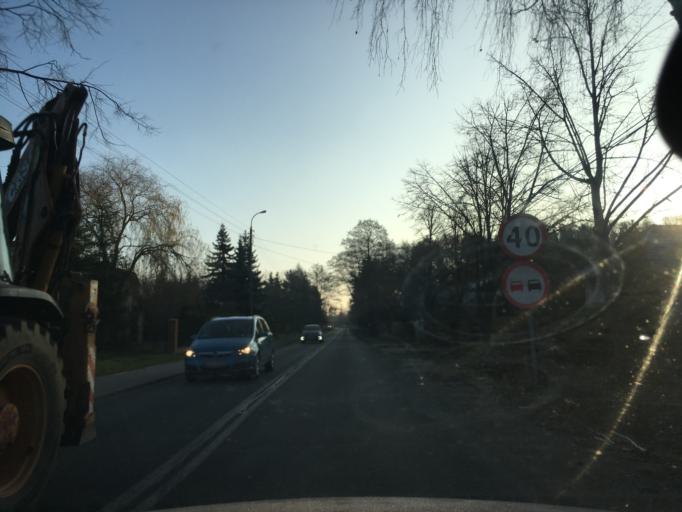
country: PL
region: Masovian Voivodeship
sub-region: Powiat piaseczynski
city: Piaseczno
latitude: 52.0711
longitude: 20.9793
